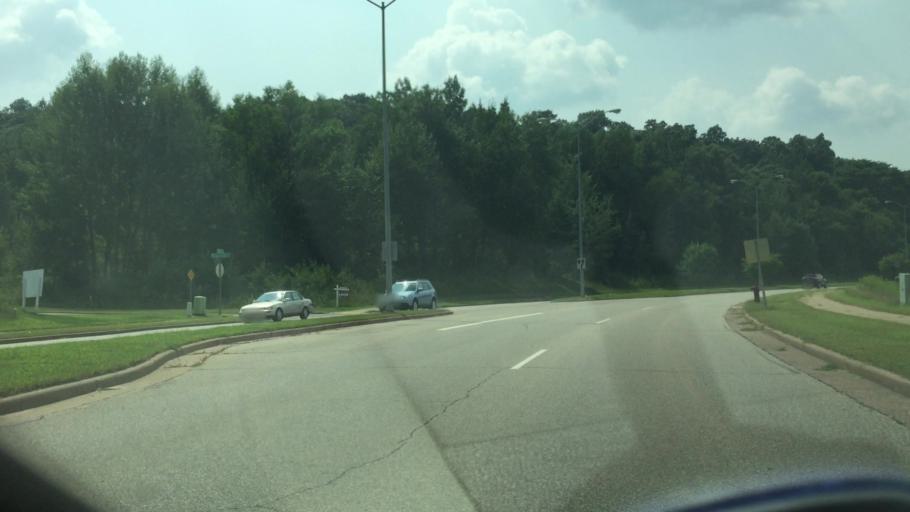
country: US
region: Wisconsin
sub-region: Eau Claire County
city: Altoona
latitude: 44.7715
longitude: -91.4397
